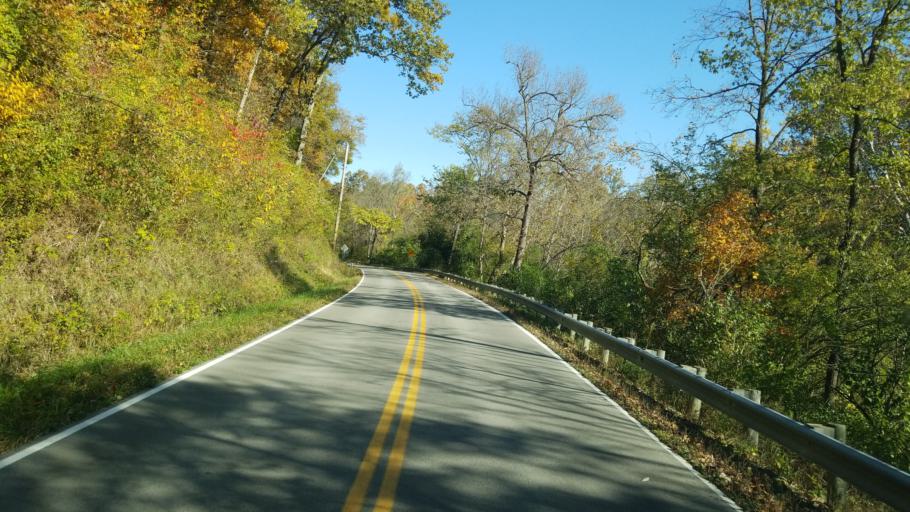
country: US
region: Ohio
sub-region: Warren County
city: Morrow
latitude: 39.3623
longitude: -84.1114
